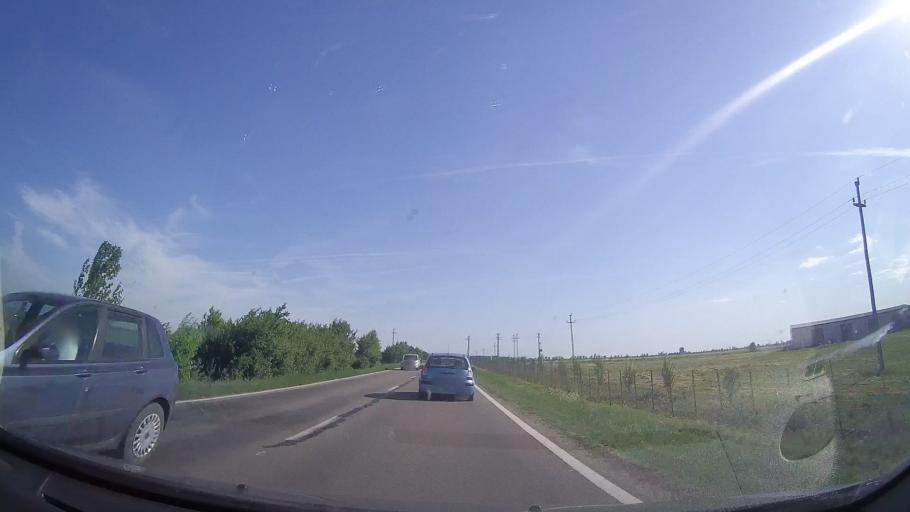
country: RO
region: Prahova
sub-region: Comuna Berceni
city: Berceni
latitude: 44.9280
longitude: 26.1032
